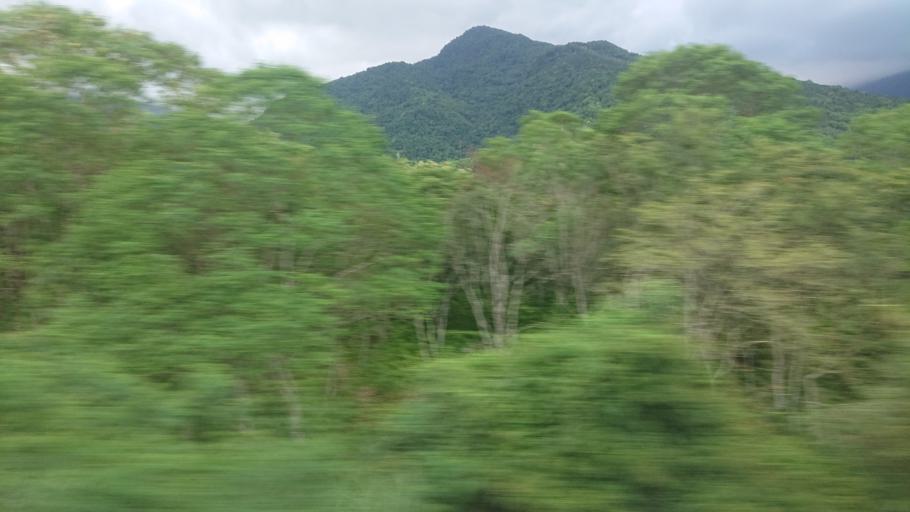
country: TW
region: Taiwan
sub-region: Hualien
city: Hualian
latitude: 23.6167
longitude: 121.3938
